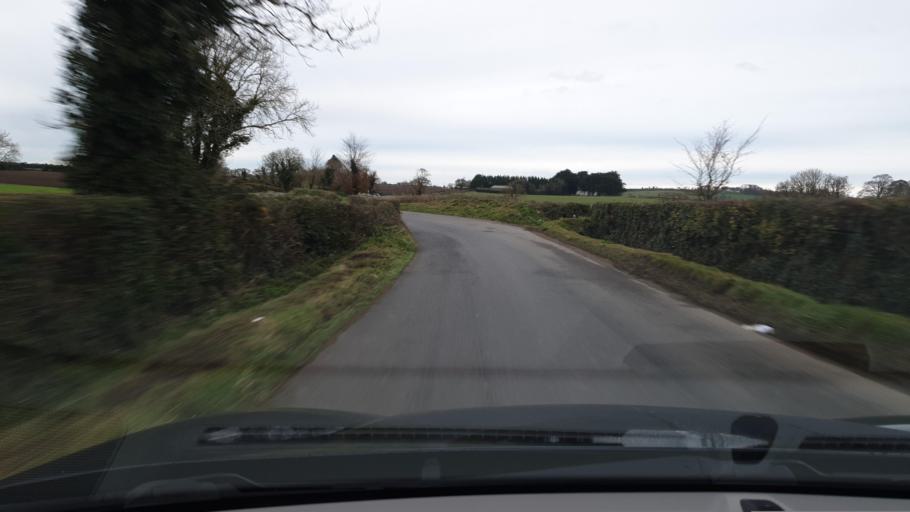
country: IE
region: Leinster
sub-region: An Mhi
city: Ashbourne
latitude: 53.5436
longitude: -6.3310
